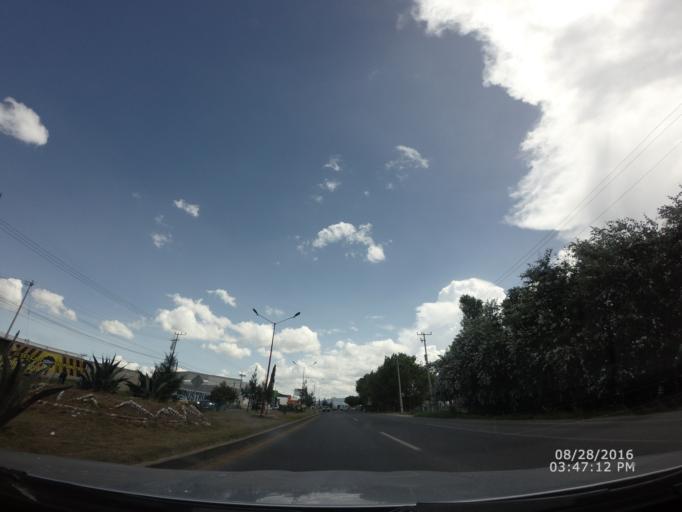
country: MX
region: Hidalgo
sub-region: Mineral de la Reforma
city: Nuevo Centro de Poblacion Agricola el Chacon
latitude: 20.0674
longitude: -98.7444
